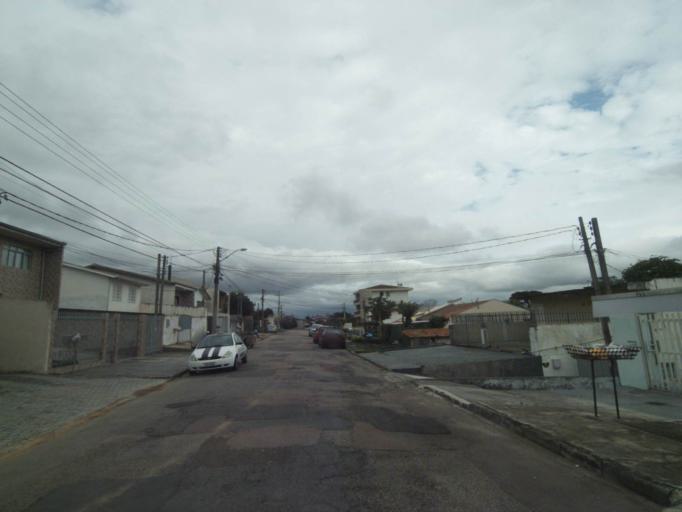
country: BR
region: Parana
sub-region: Curitiba
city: Curitiba
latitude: -25.4861
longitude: -49.2901
